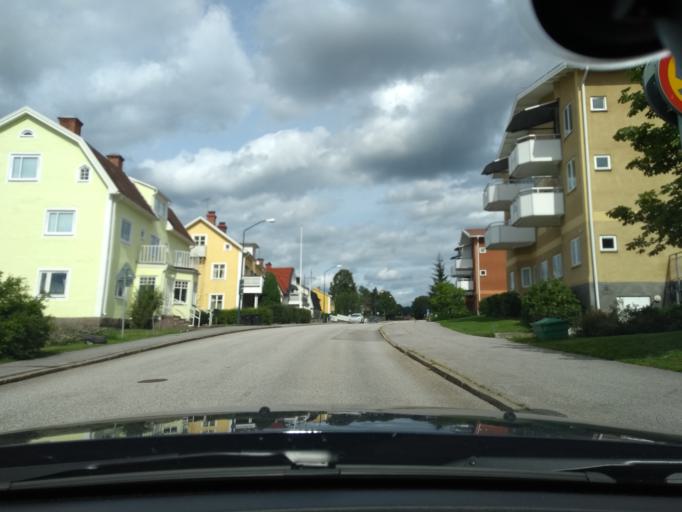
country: SE
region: Kalmar
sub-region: Vimmerby Kommun
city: Vimmerby
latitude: 57.6694
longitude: 15.8582
